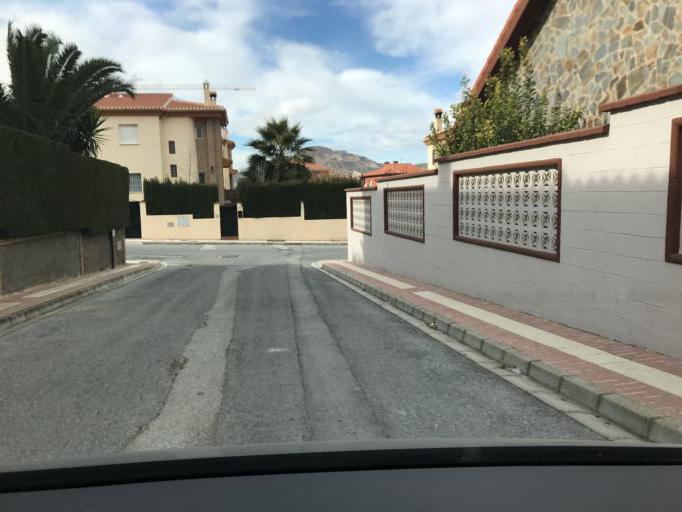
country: ES
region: Andalusia
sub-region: Provincia de Granada
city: Alhendin
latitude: 37.1053
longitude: -3.6607
